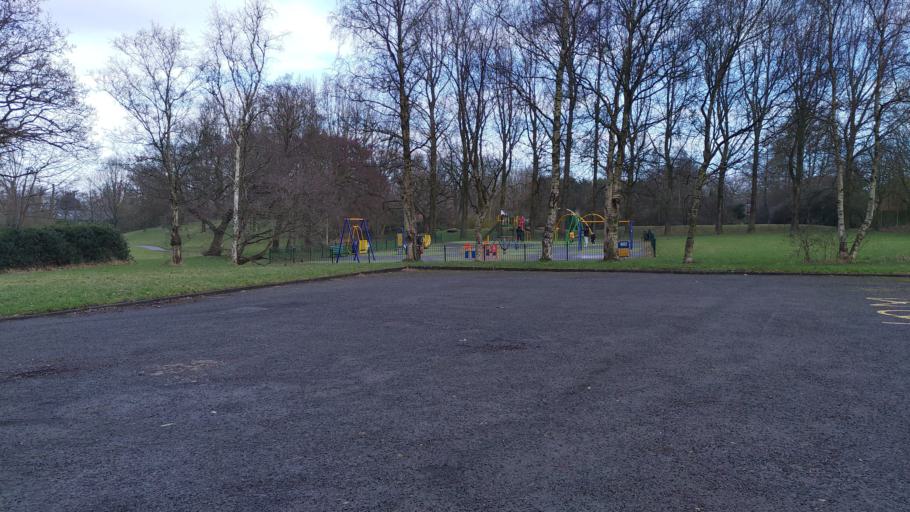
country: GB
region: England
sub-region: Lancashire
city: Clayton-le-Woods
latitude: 53.7128
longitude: -2.6362
